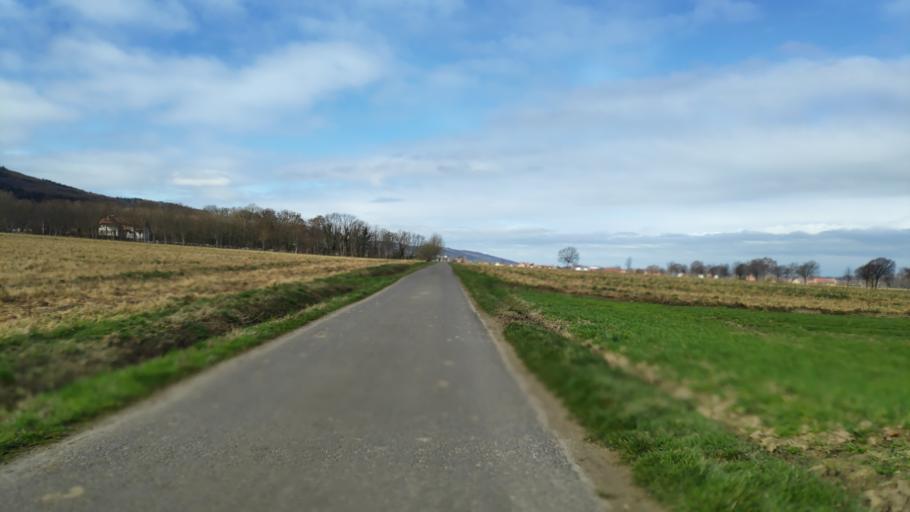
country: DE
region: North Rhine-Westphalia
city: Bad Oeynhausen
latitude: 52.2688
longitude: 8.8146
